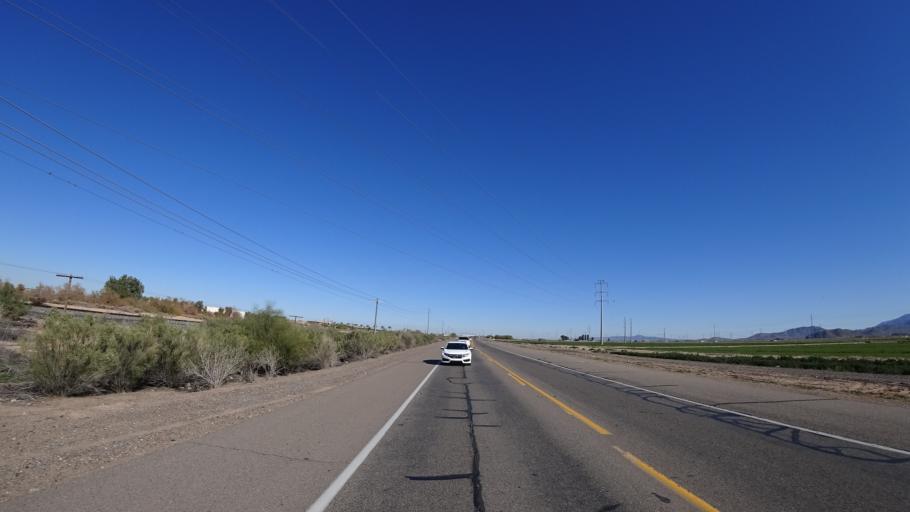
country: US
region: Arizona
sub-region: Maricopa County
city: Goodyear
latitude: 33.4081
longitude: -112.3979
